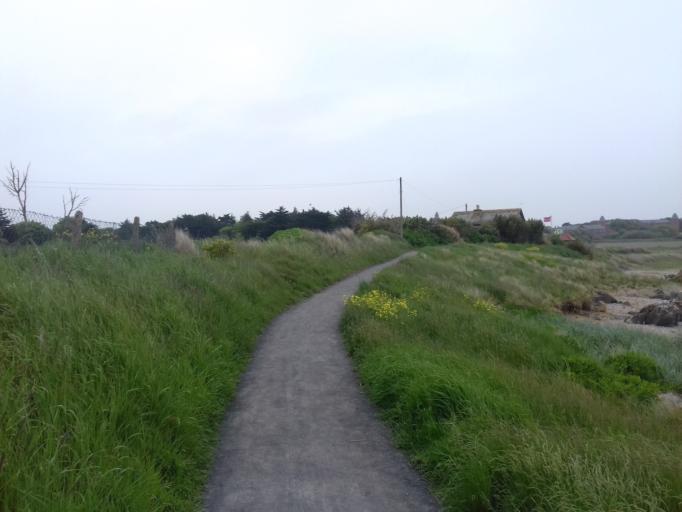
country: IE
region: Leinster
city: Portraine
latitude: 53.4806
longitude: -6.1135
